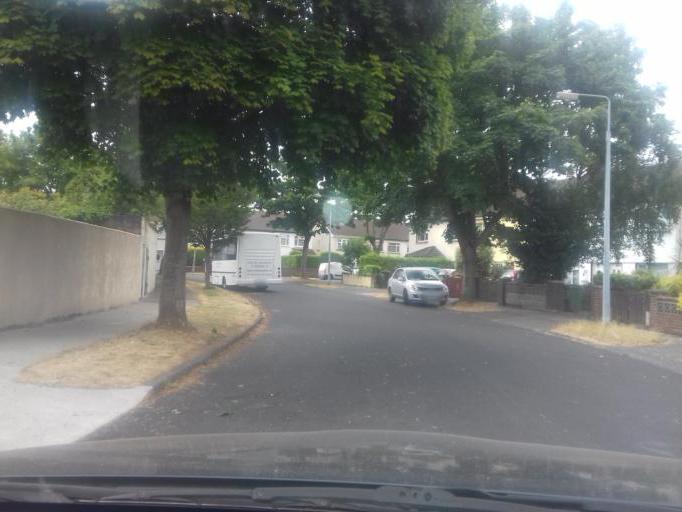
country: IE
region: Leinster
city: Hartstown
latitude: 53.4017
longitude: -6.4123
